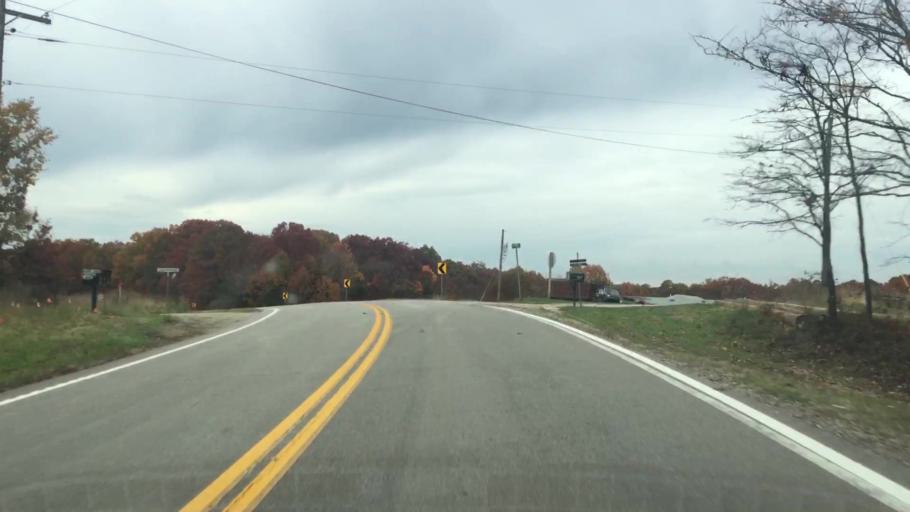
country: US
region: Missouri
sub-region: Gasconade County
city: Hermann
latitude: 38.7179
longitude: -91.6419
